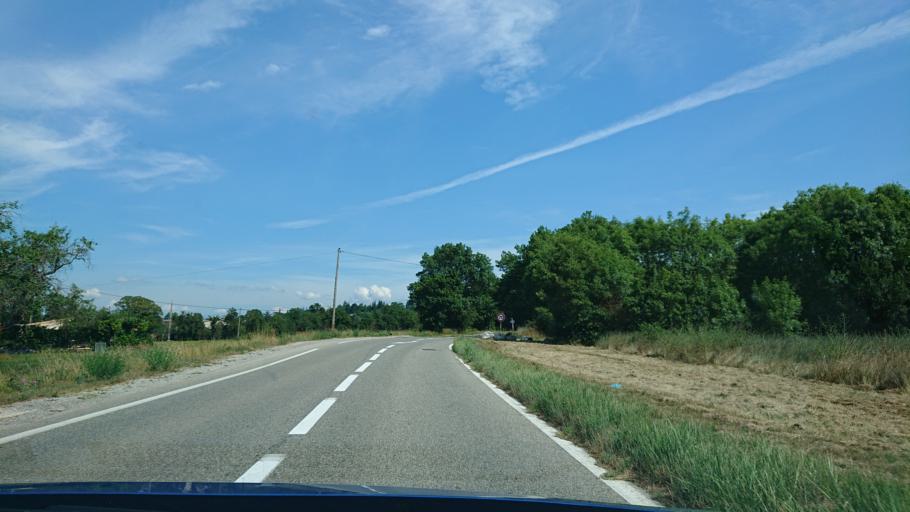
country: FR
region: Provence-Alpes-Cote d'Azur
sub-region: Departement des Alpes-de-Haute-Provence
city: Sisteron
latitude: 44.2127
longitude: 5.9403
